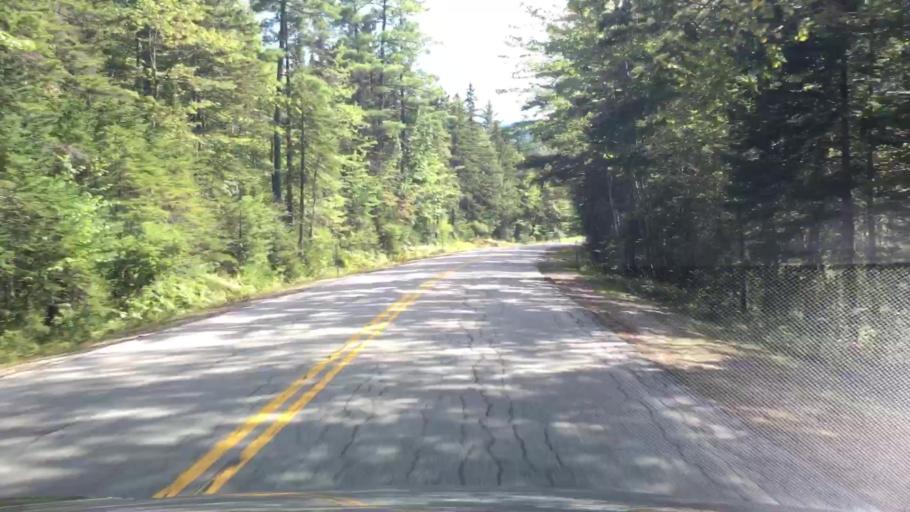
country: US
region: New Hampshire
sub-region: Carroll County
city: Tamworth
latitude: 44.0043
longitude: -71.3206
